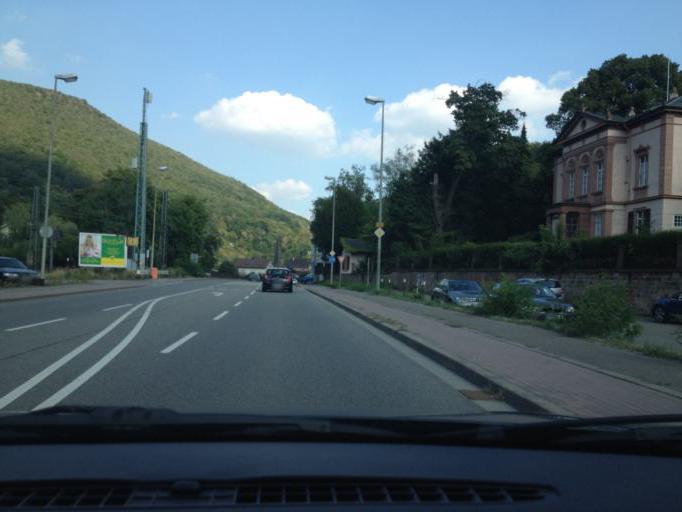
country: DE
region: Rheinland-Pfalz
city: Lindenberg
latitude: 49.3562
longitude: 8.1094
